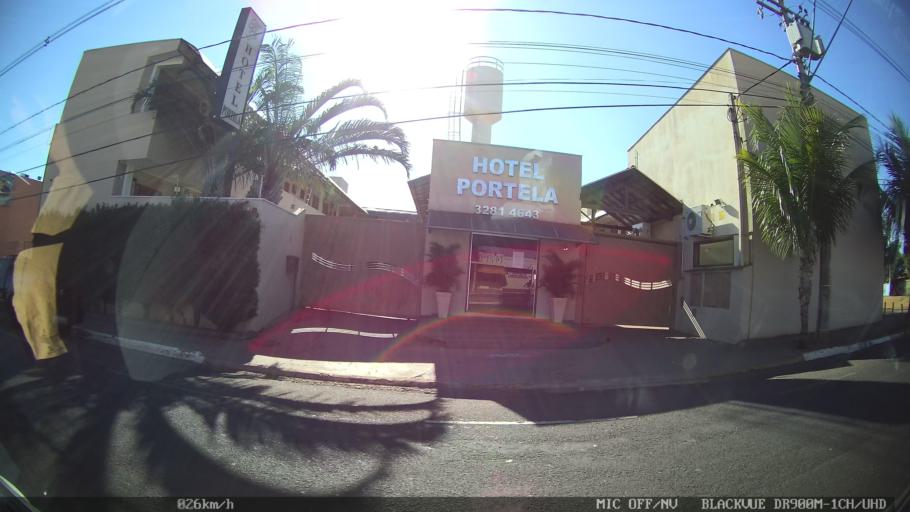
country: BR
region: Sao Paulo
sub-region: Olimpia
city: Olimpia
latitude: -20.7262
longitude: -48.9120
